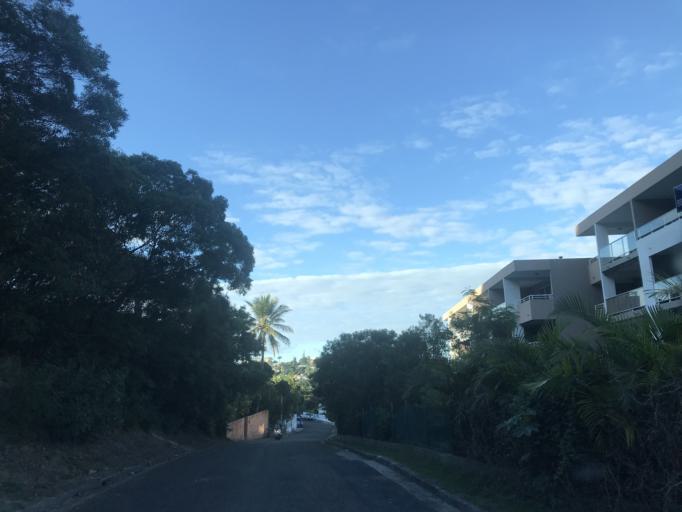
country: NC
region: South Province
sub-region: Noumea
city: Noumea
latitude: -22.2664
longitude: 166.4496
